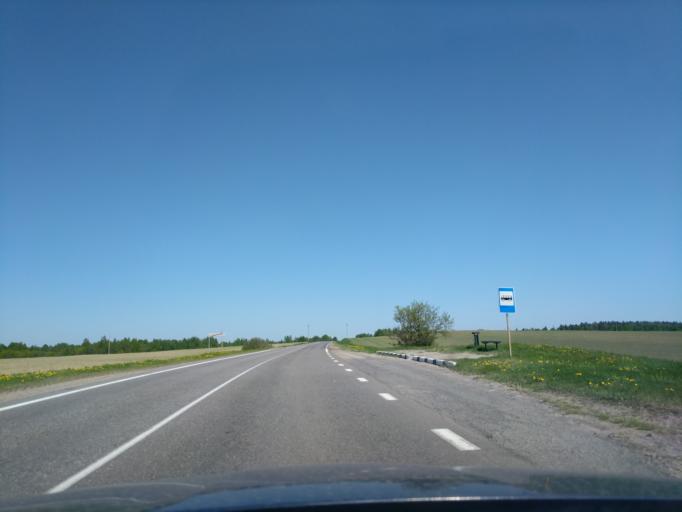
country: BY
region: Minsk
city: Il'ya
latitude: 54.2994
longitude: 27.4782
